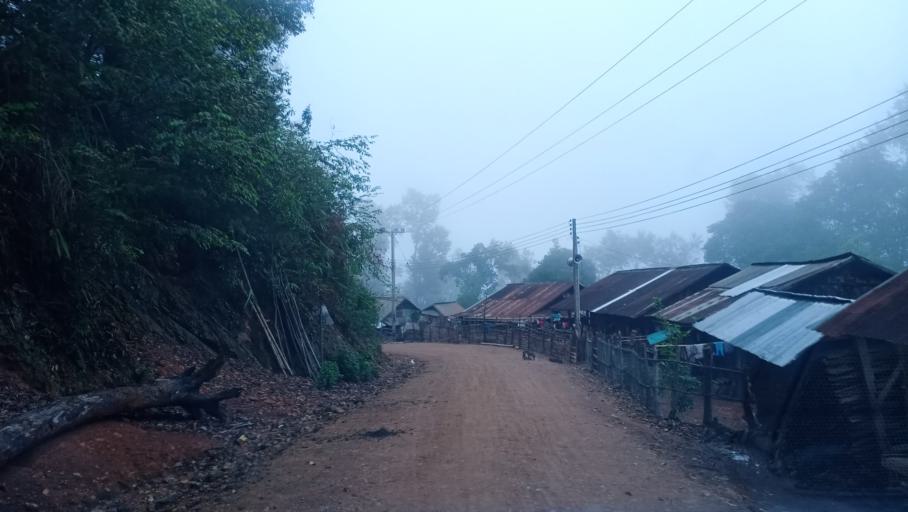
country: LA
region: Phongsali
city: Phongsali
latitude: 21.5342
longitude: 102.2204
